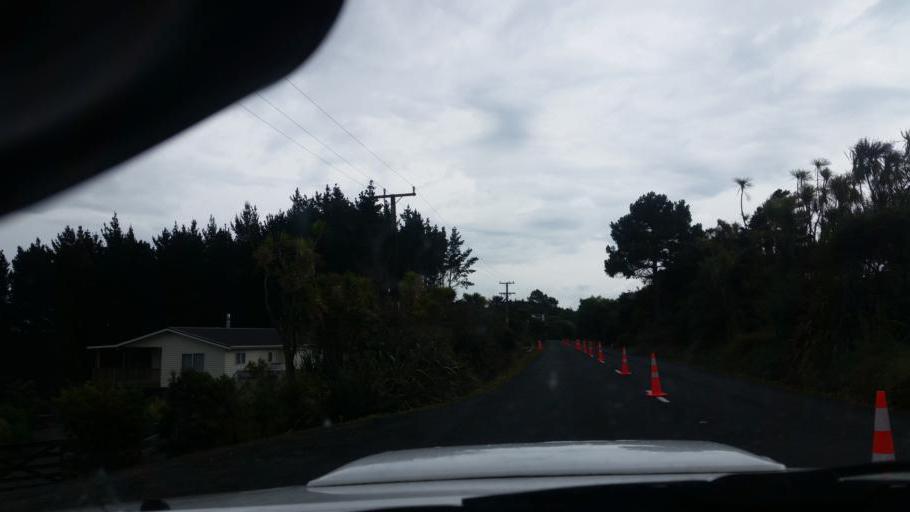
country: NZ
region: Auckland
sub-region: Auckland
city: Wellsford
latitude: -36.1456
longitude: 174.2239
